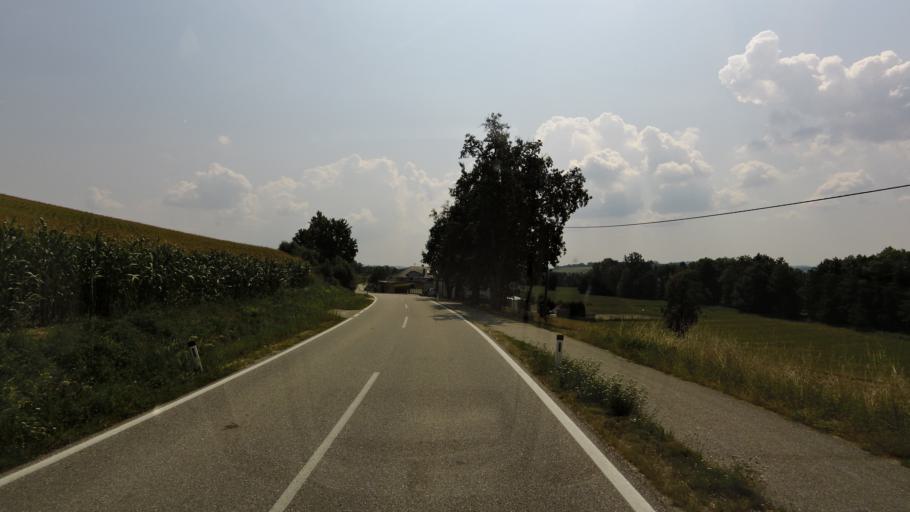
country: AT
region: Upper Austria
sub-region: Politischer Bezirk Ried im Innkreis
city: Waldzell
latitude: 48.2021
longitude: 13.3713
